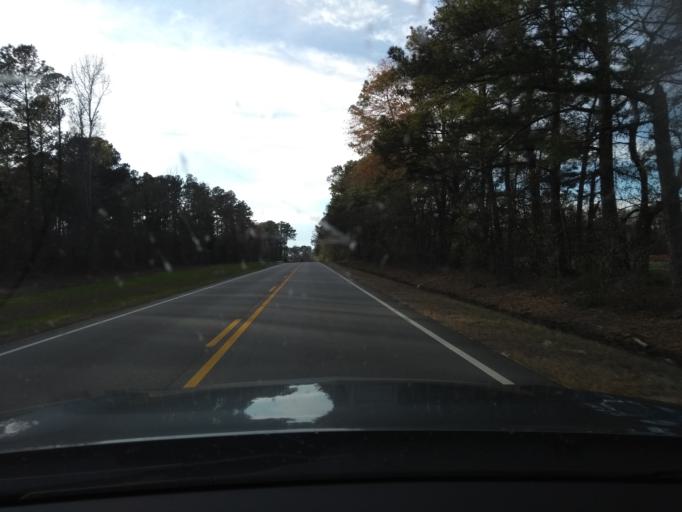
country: US
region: Georgia
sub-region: Bulloch County
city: Brooklet
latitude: 32.2910
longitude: -81.7629
